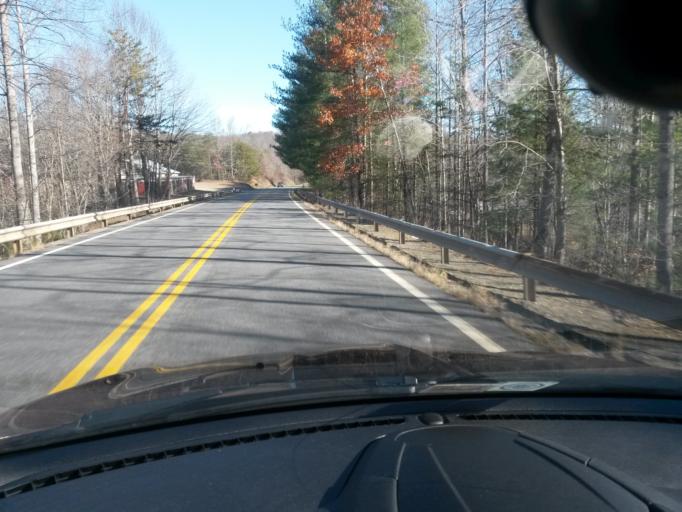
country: US
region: Virginia
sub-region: Patrick County
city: Patrick Springs
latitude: 36.7322
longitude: -80.2220
